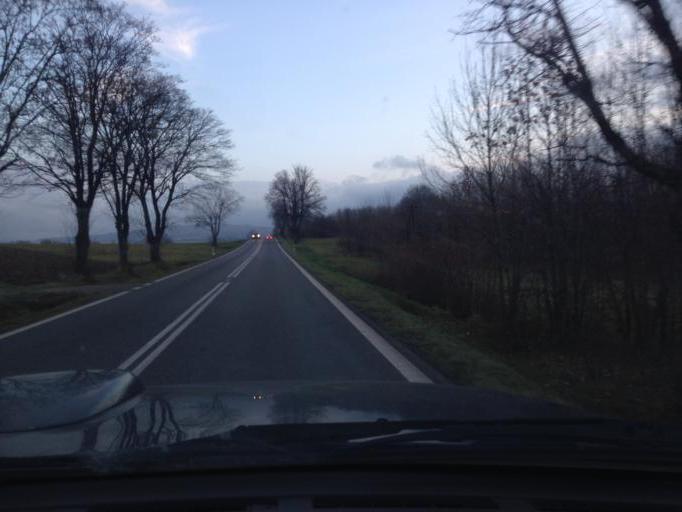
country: PL
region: Subcarpathian Voivodeship
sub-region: Powiat jasielski
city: Nowy Zmigrod
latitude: 49.6279
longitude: 21.5327
